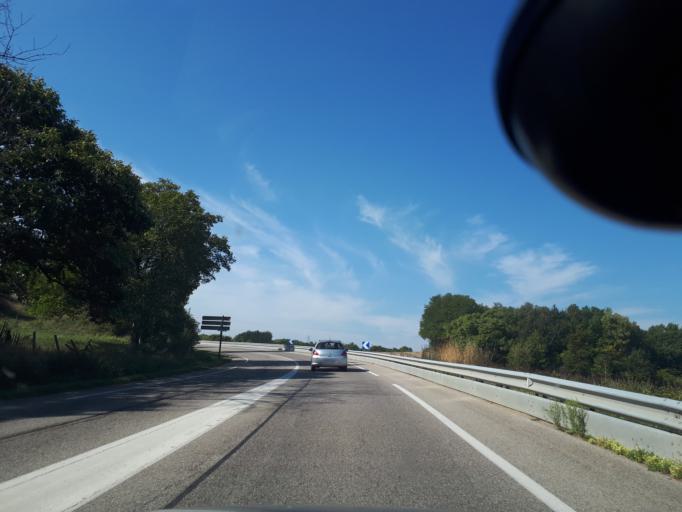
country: FR
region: Rhone-Alpes
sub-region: Departement de l'Isere
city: Maubec
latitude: 45.5386
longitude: 5.2296
